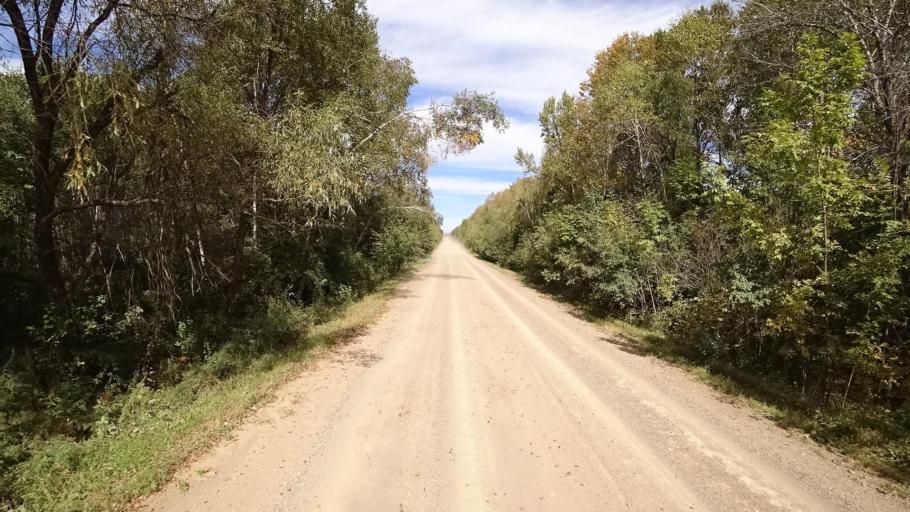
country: RU
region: Primorskiy
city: Yakovlevka
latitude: 44.6838
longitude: 133.6176
